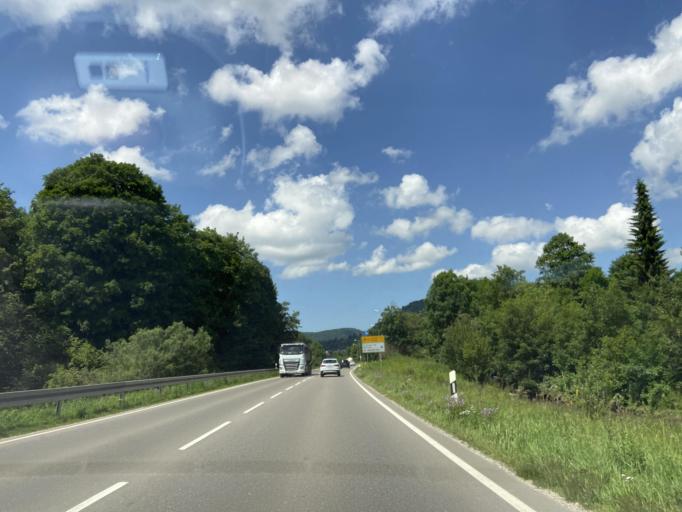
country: DE
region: Baden-Wuerttemberg
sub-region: Tuebingen Region
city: Albstadt
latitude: 48.1995
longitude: 9.0494
